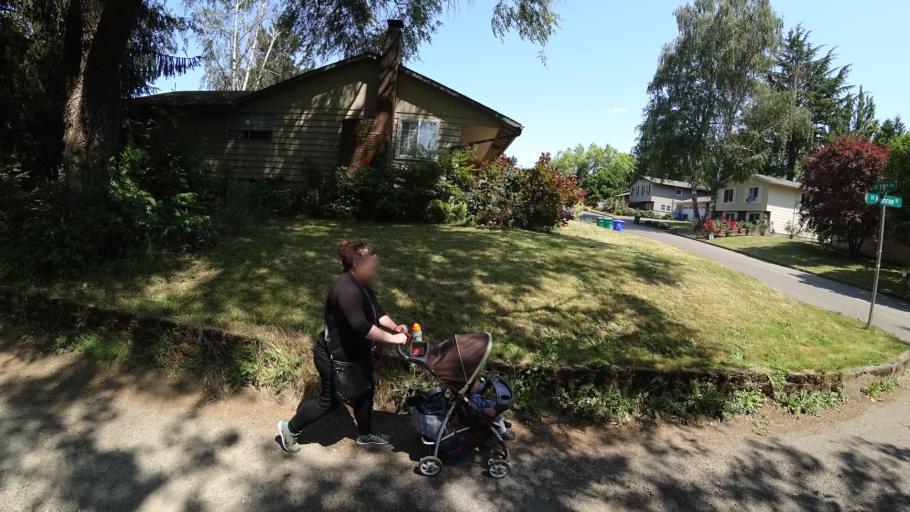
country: US
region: Oregon
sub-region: Clackamas County
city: Oatfield
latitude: 45.4447
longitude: -122.5837
